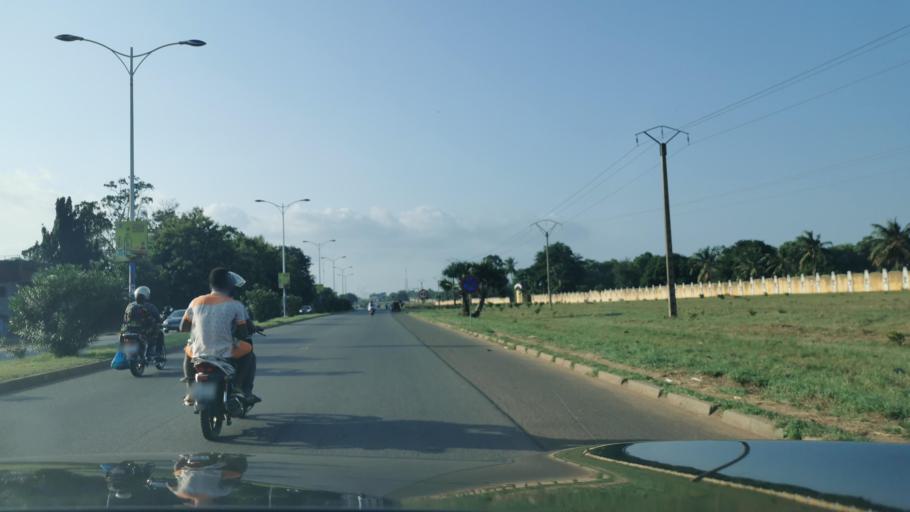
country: TG
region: Maritime
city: Lome
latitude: 6.2062
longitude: 1.2087
